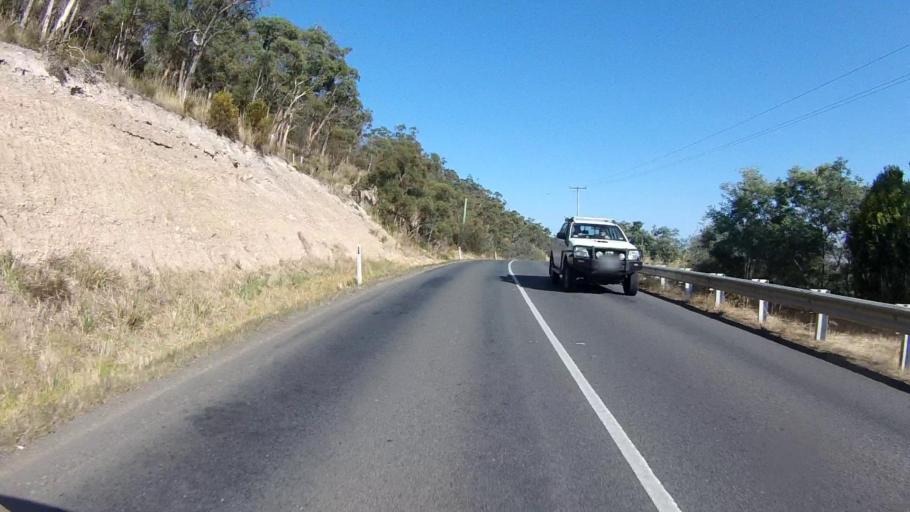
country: AU
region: Tasmania
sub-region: Derwent Valley
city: New Norfolk
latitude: -42.7815
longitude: 147.0396
